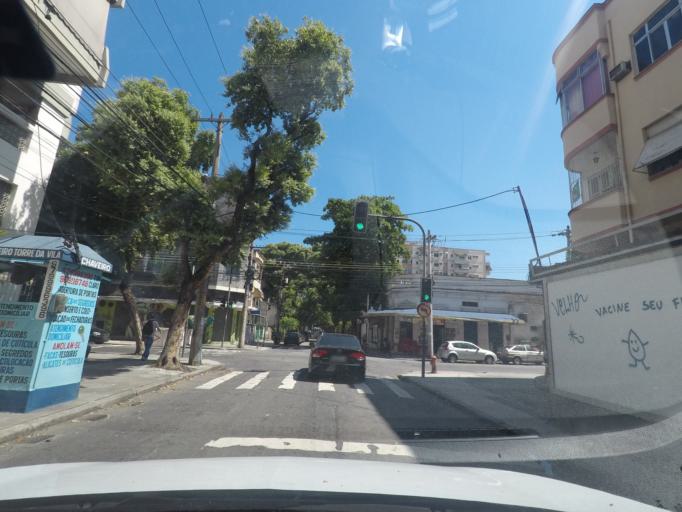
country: BR
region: Rio de Janeiro
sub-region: Rio De Janeiro
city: Rio de Janeiro
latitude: -22.9140
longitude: -43.2481
